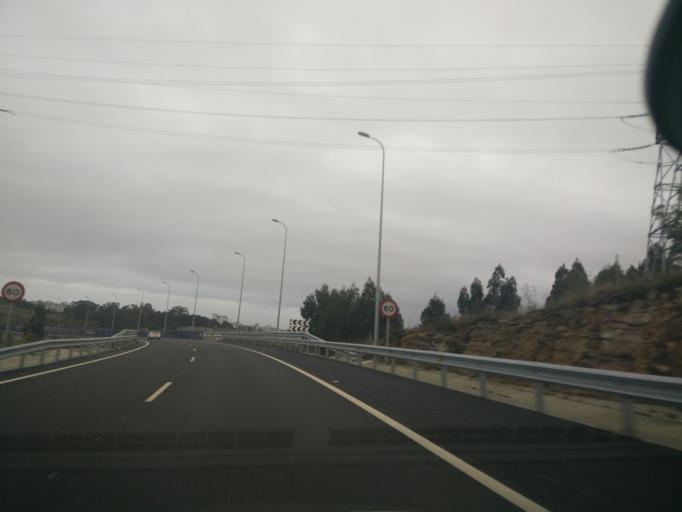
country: ES
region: Galicia
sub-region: Provincia da Coruna
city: A Coruna
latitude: 43.3341
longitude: -8.4207
